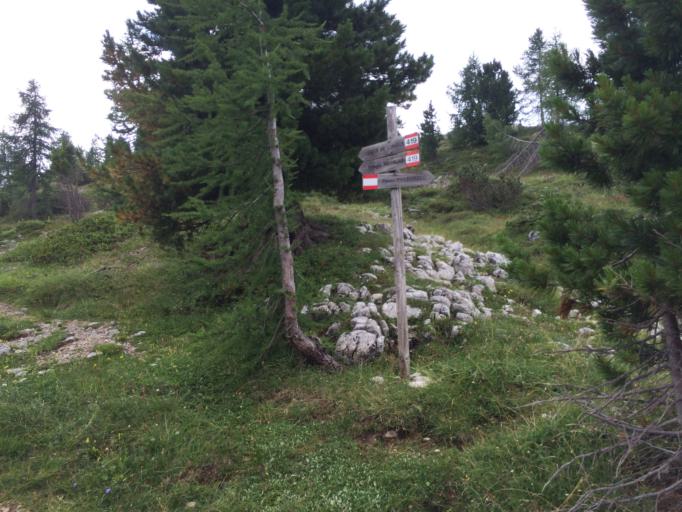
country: IT
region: Veneto
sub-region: Provincia di Belluno
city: Colle Santa Lucia
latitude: 46.5140
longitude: 12.0197
